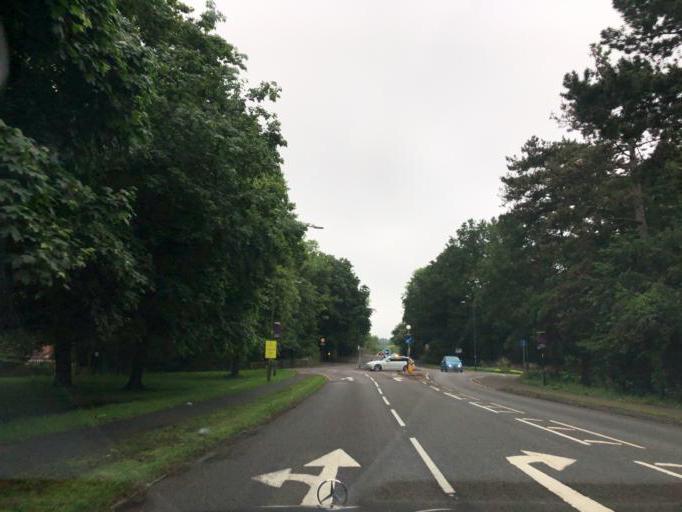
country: GB
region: England
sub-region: Warwickshire
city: Warwick
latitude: 52.2782
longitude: -1.5781
